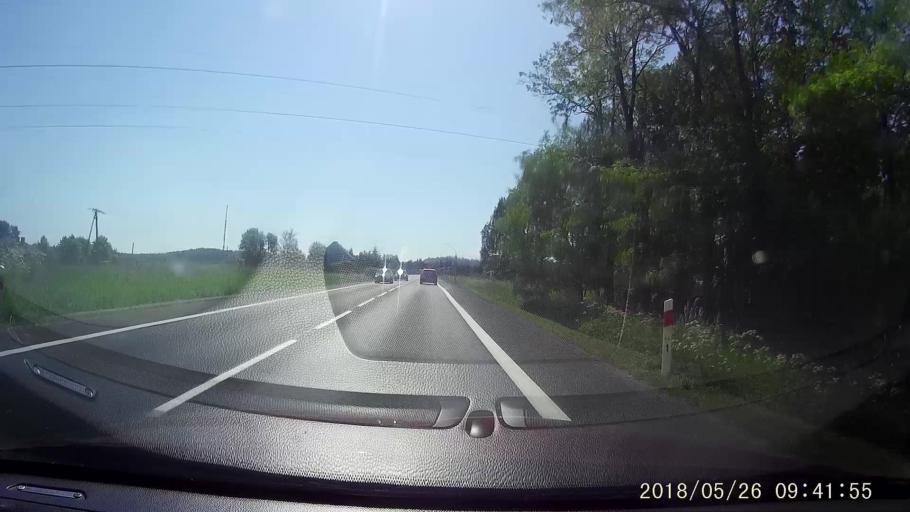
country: PL
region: Lower Silesian Voivodeship
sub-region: Powiat lubanski
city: Siekierczyn
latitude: 51.1604
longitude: 15.1526
